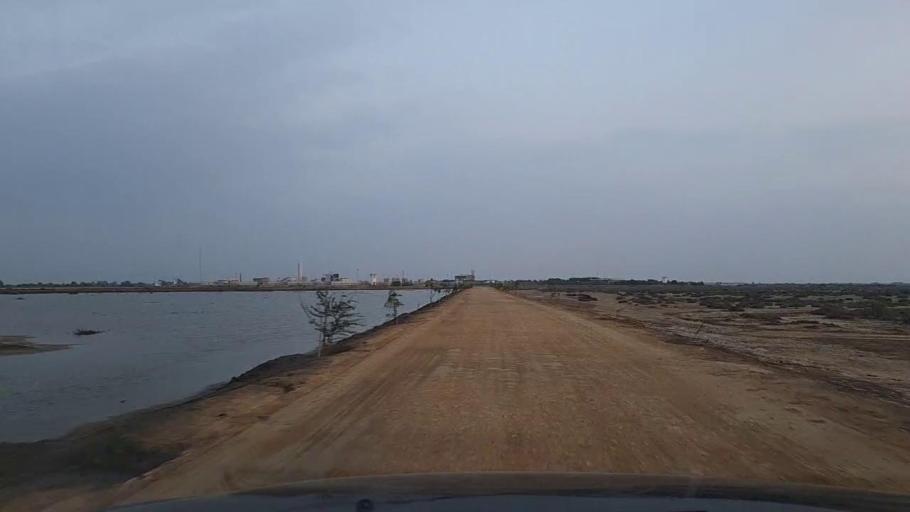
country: PK
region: Sindh
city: Jati
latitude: 24.4934
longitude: 68.3888
